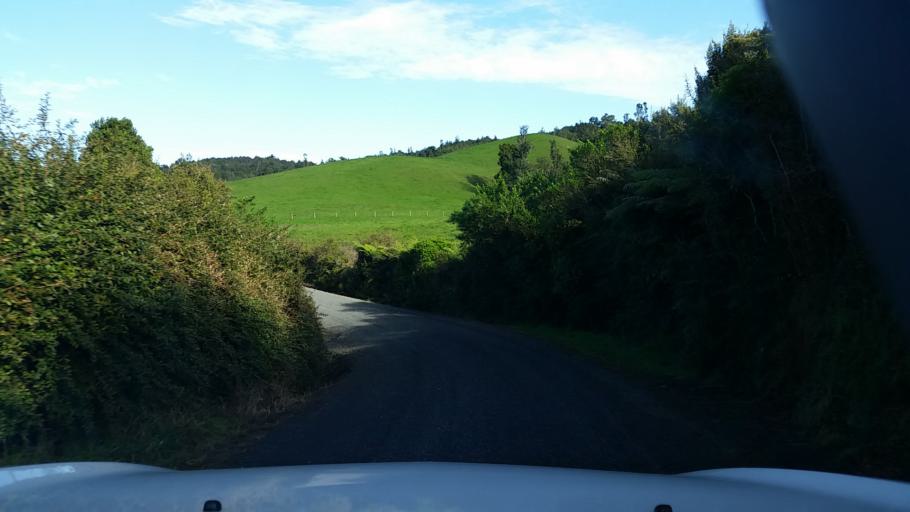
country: NZ
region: Waikato
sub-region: Matamata-Piako District
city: Matamata
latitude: -37.8190
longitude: 175.6317
